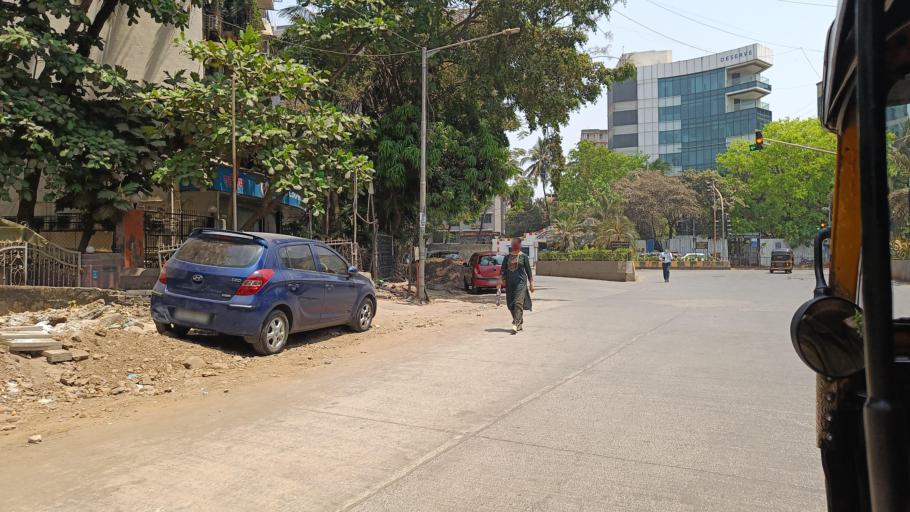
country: IN
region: Maharashtra
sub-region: Mumbai Suburban
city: Mumbai
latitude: 19.0746
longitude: 72.8600
